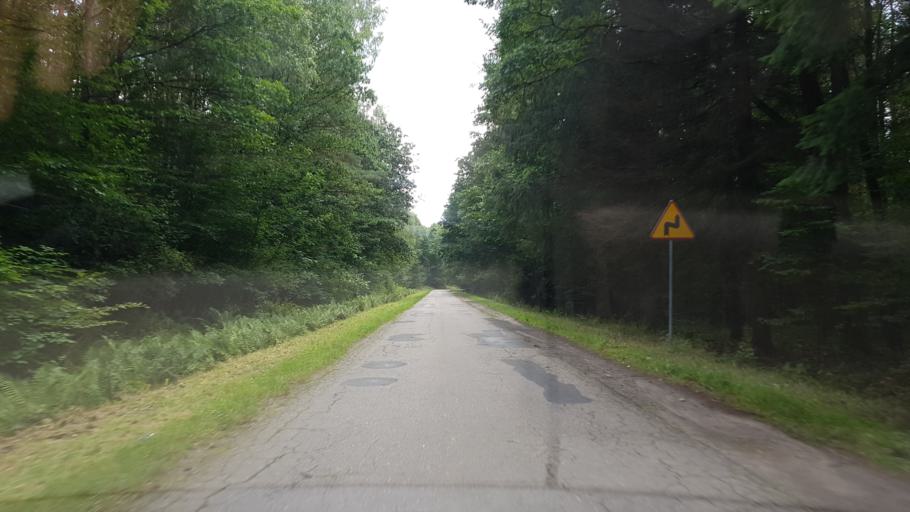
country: PL
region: West Pomeranian Voivodeship
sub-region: Powiat bialogardzki
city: Tychowo
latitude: 53.9728
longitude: 16.3148
